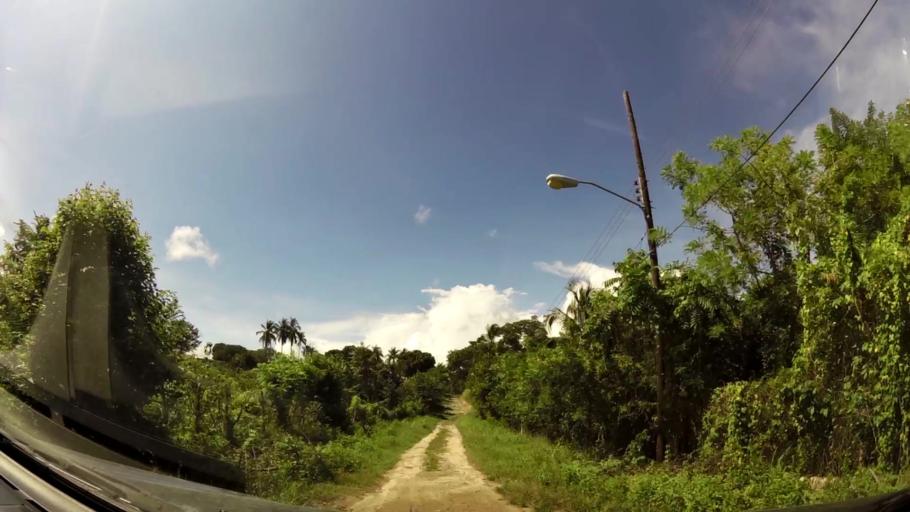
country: PA
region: Panama
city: Nueva Gorgona
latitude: 8.5554
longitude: -79.8650
